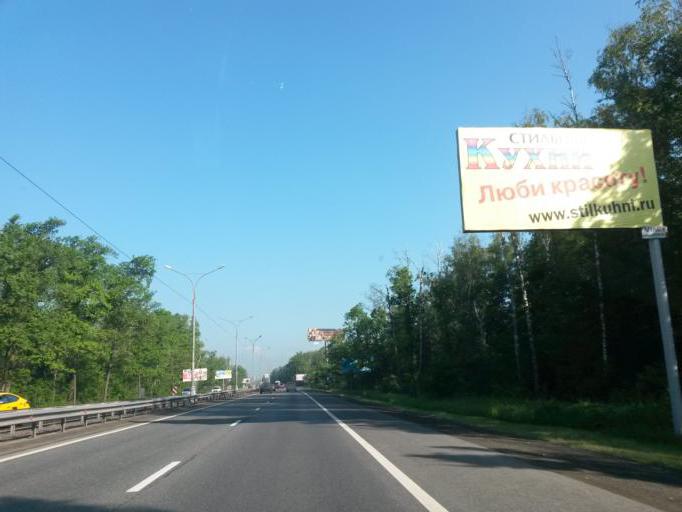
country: RU
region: Moskovskaya
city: Petrovskaya
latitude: 55.5473
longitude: 37.7948
